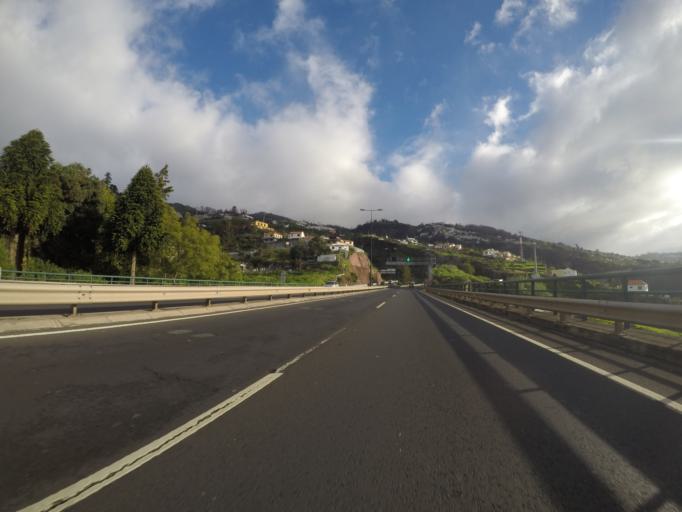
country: PT
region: Madeira
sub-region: Funchal
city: Nossa Senhora do Monte
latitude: 32.6623
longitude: -16.9035
